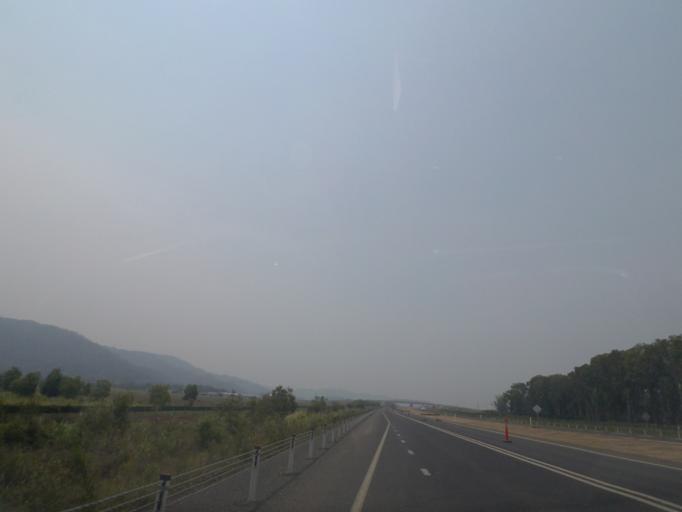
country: AU
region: New South Wales
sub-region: Ballina
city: Ballina
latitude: -28.9070
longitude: 153.4788
